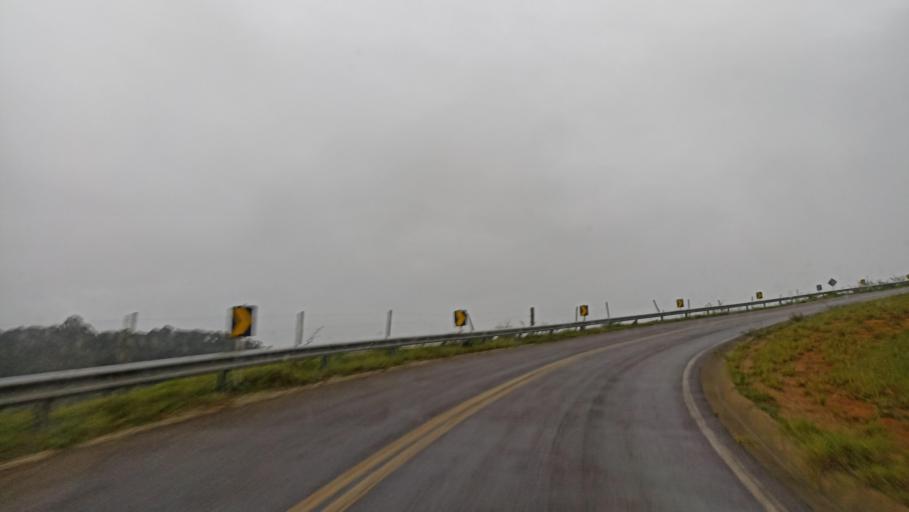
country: BR
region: Bahia
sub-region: Itanhem
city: Itanhem
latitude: -16.7320
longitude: -40.4372
